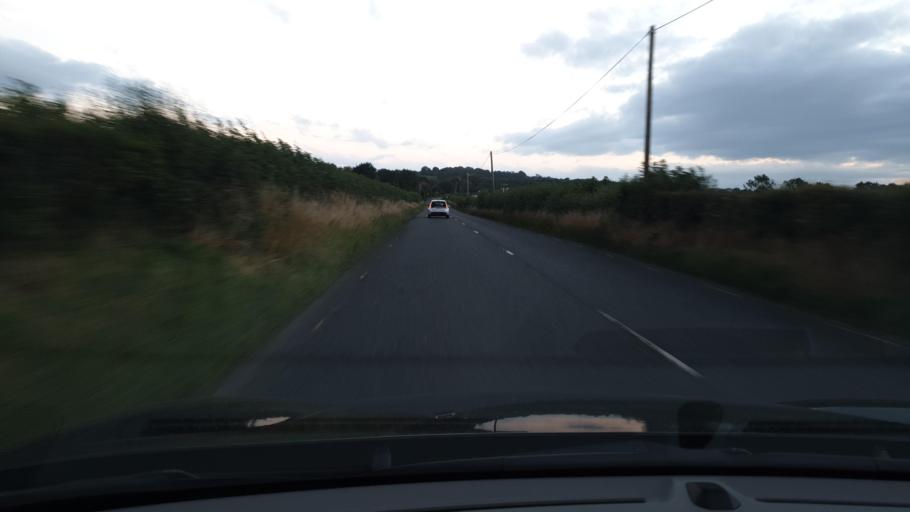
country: IE
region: Leinster
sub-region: An Mhi
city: Duleek
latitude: 53.6178
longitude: -6.4259
